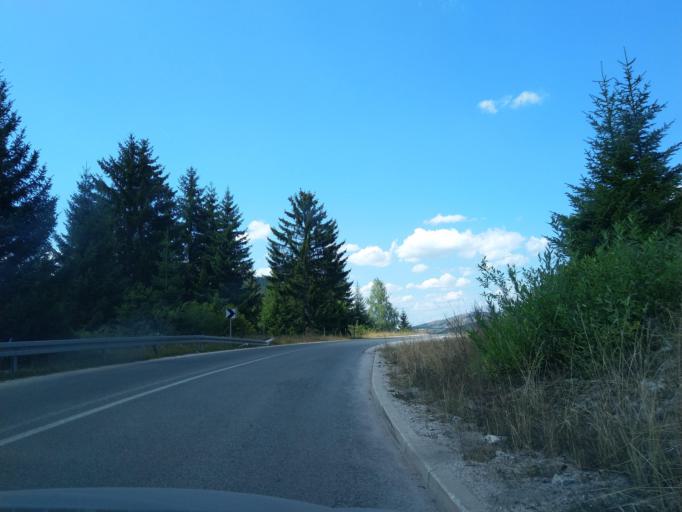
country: RS
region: Central Serbia
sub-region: Zlatiborski Okrug
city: Nova Varos
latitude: 43.4286
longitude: 19.8290
